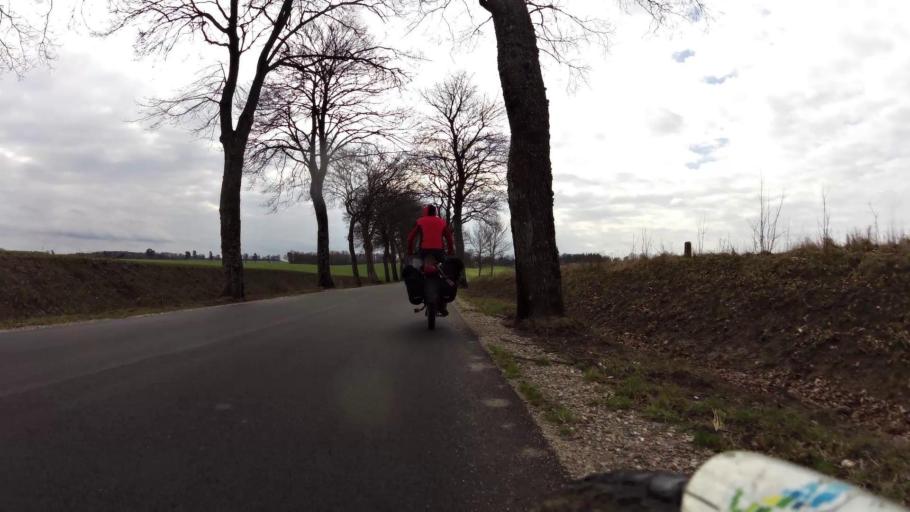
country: PL
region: Pomeranian Voivodeship
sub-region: Powiat bytowski
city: Kolczyglowy
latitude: 54.2299
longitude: 17.2420
